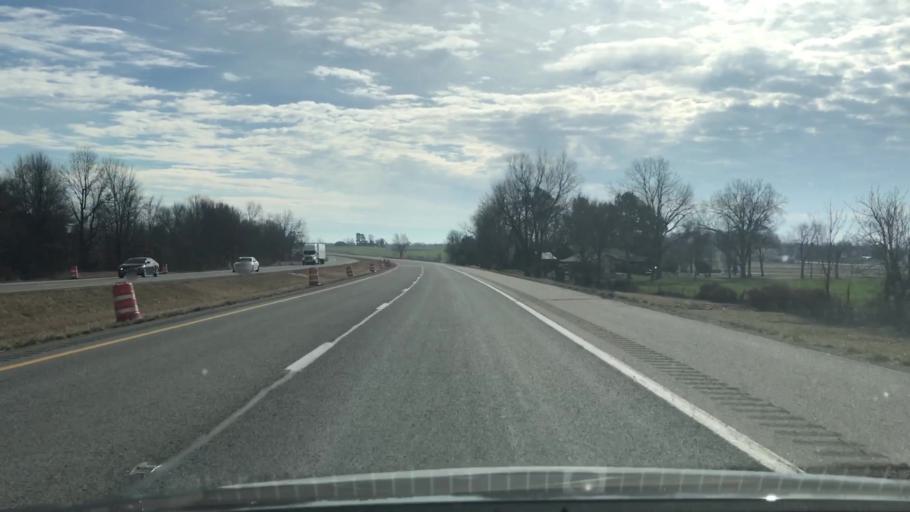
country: US
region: Kentucky
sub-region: Daviess County
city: Masonville
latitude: 37.6709
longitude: -87.0252
